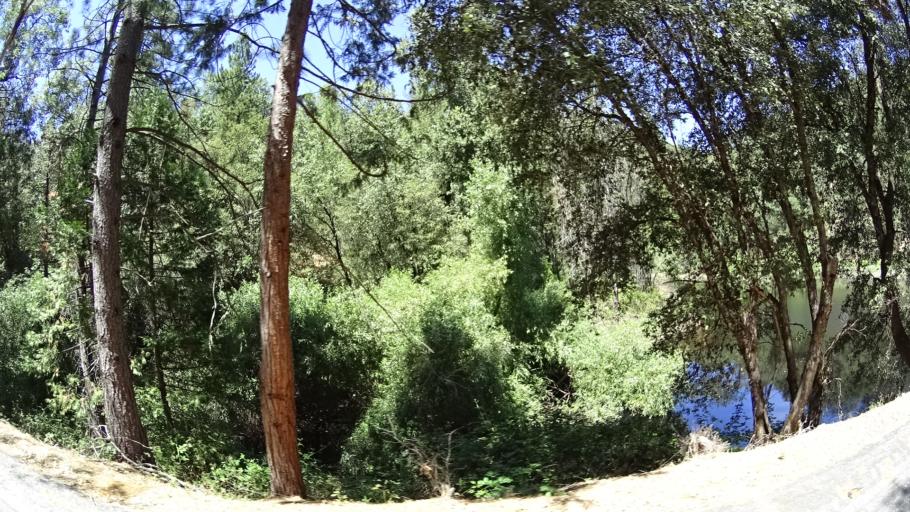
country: US
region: California
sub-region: Calaveras County
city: Forest Meadows
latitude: 38.2160
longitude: -120.4370
